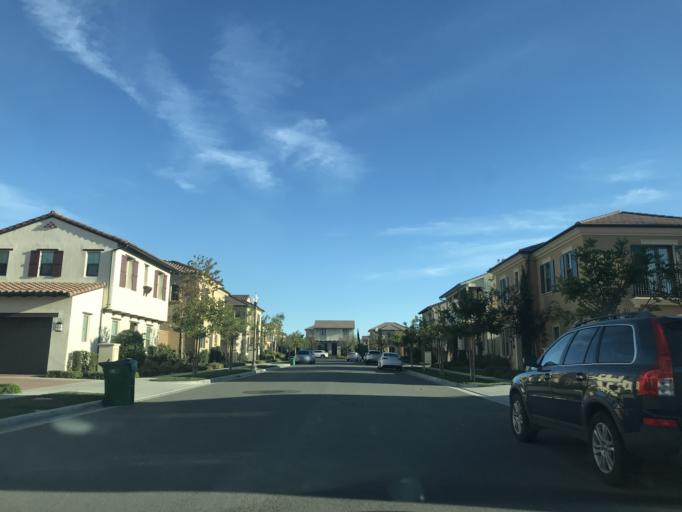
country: US
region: California
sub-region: Orange County
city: North Tustin
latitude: 33.7139
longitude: -117.7546
